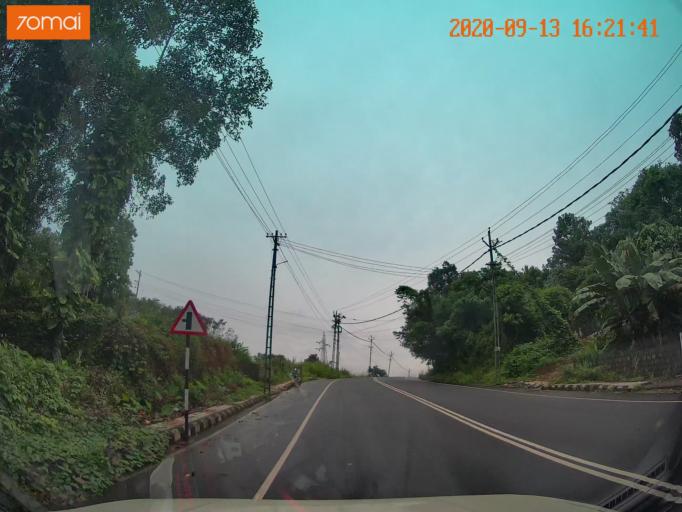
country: IN
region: Kerala
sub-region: Kottayam
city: Lalam
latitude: 9.7100
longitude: 76.6674
